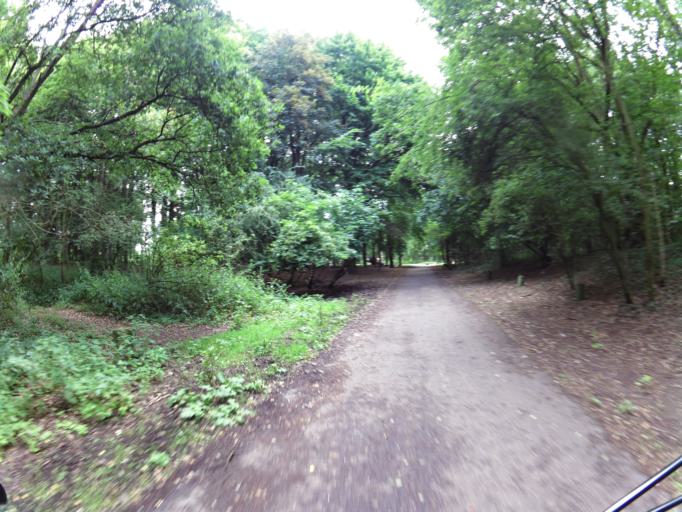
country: NL
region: Limburg
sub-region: Gemeente Brunssum
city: Brunssum
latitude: 50.9243
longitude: 5.9784
